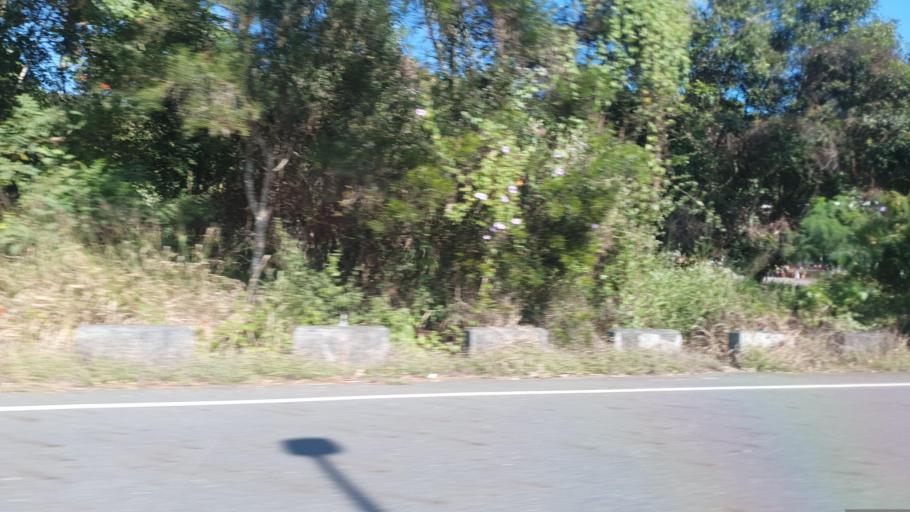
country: TW
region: Taiwan
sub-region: Tainan
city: Tainan
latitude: 23.0381
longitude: 120.3370
